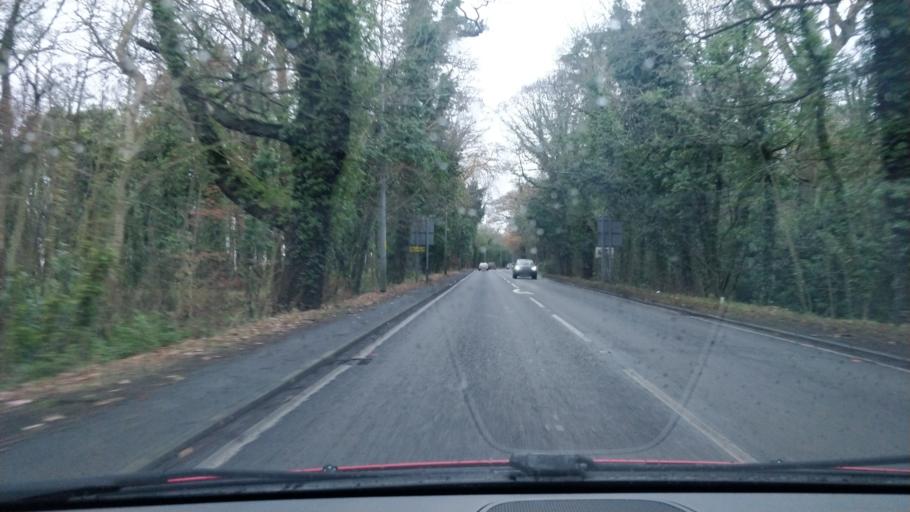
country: GB
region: England
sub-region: Sefton
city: Ince Blundell
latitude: 53.5168
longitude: -3.0204
